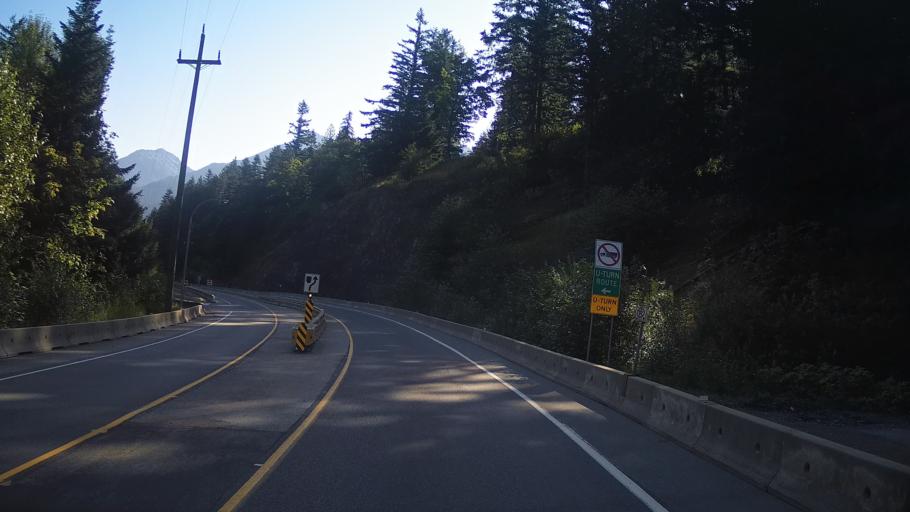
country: CA
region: British Columbia
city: Hope
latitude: 49.4088
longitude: -121.4470
